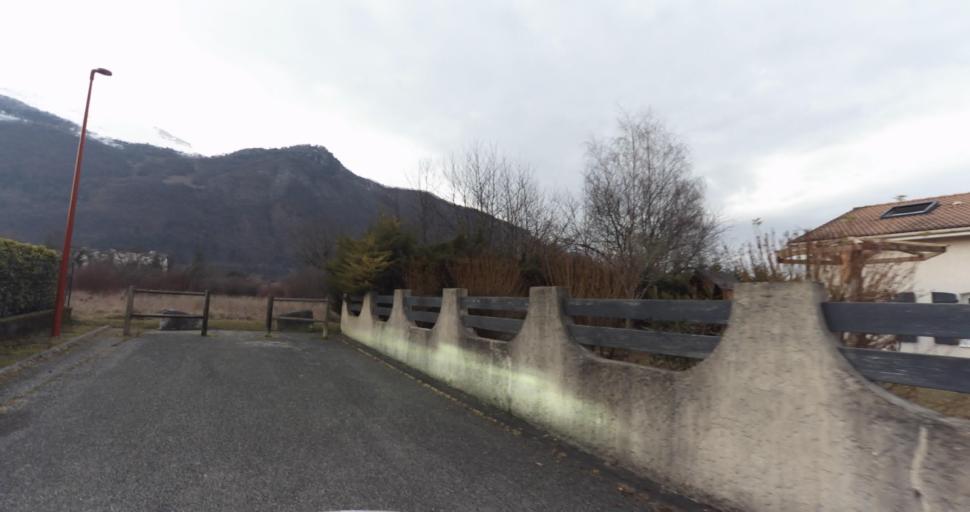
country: FR
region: Rhone-Alpes
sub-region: Departement de l'Isere
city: Vif
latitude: 45.0579
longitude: 5.6755
